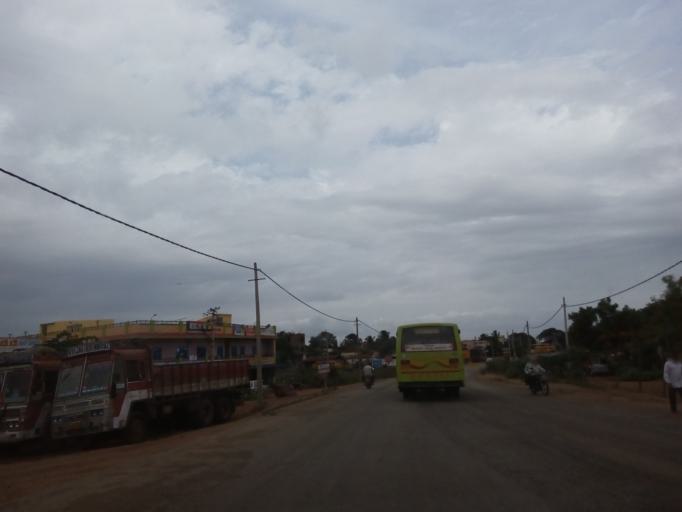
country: IN
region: Karnataka
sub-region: Davanagere
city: Harihar
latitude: 14.5196
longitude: 75.7876
